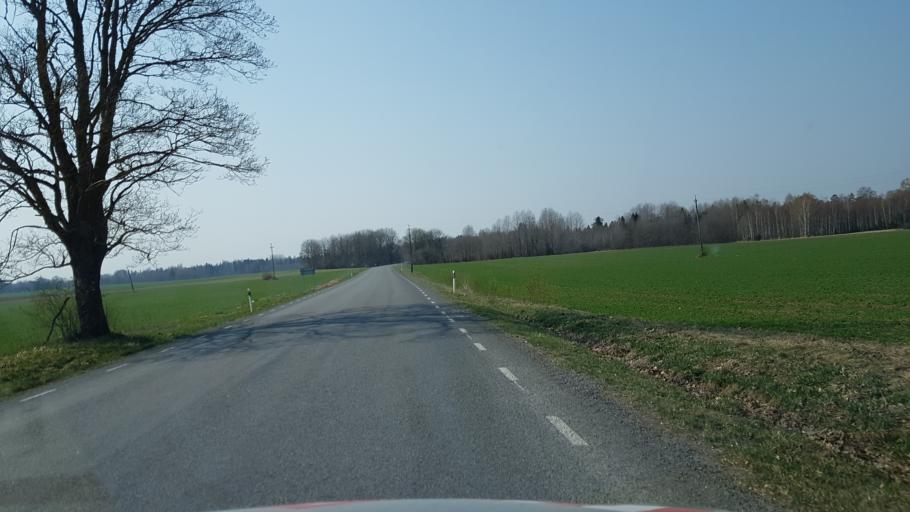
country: EE
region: Raplamaa
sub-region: Kehtna vald
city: Kehtna
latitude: 59.0399
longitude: 24.9364
